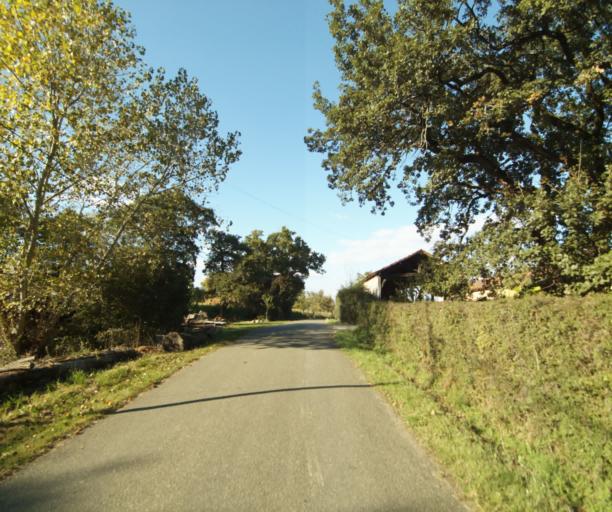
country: FR
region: Midi-Pyrenees
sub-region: Departement du Gers
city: Eauze
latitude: 43.7958
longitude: 0.1348
